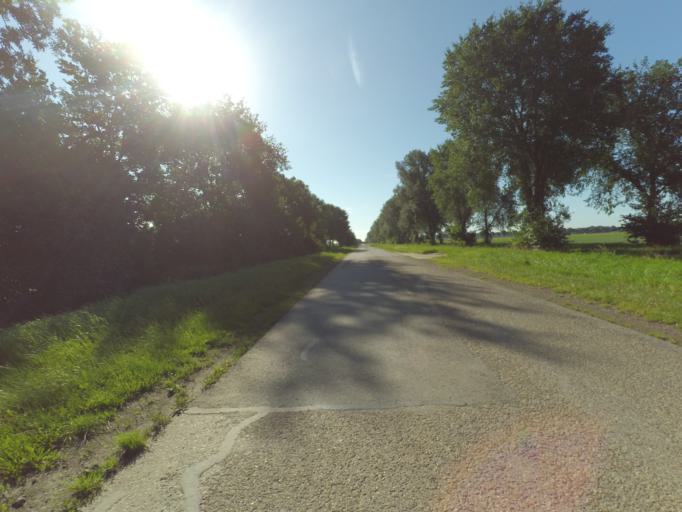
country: NL
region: Flevoland
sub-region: Gemeente Zeewolde
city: Zeewolde
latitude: 52.3812
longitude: 5.5018
